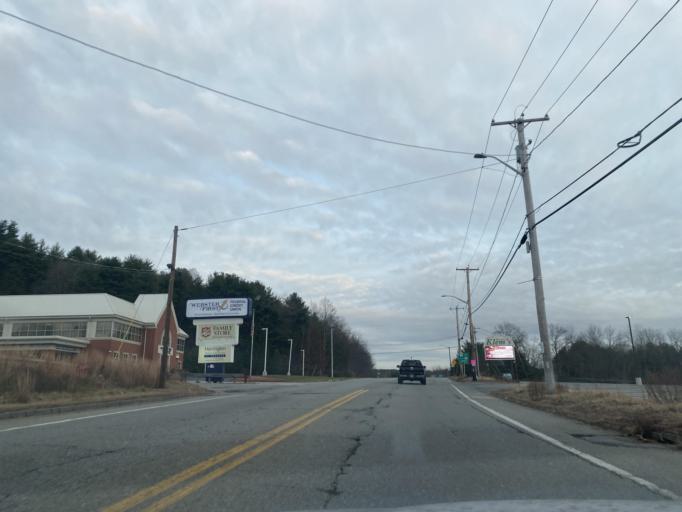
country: US
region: Massachusetts
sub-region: Worcester County
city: East Brookfield
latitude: 42.2316
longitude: -72.0236
